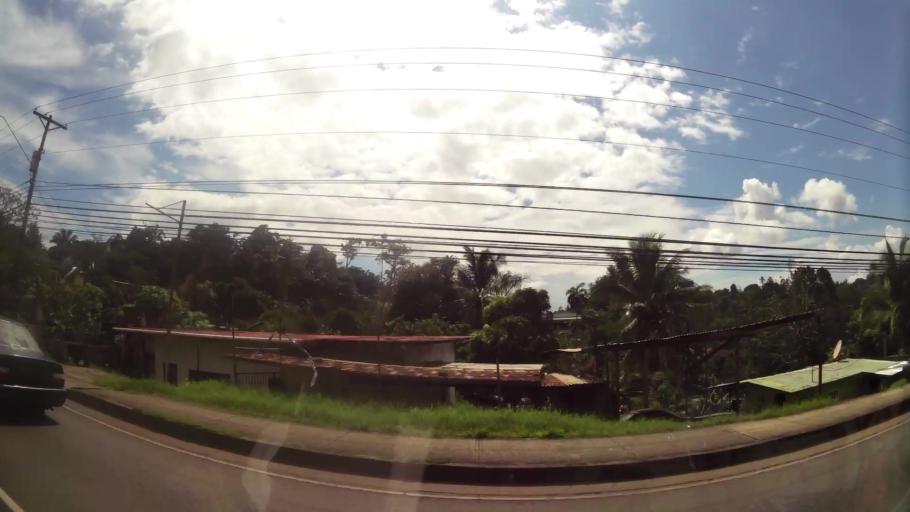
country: PA
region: Panama
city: Vista Alegre
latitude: 8.9338
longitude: -79.6907
